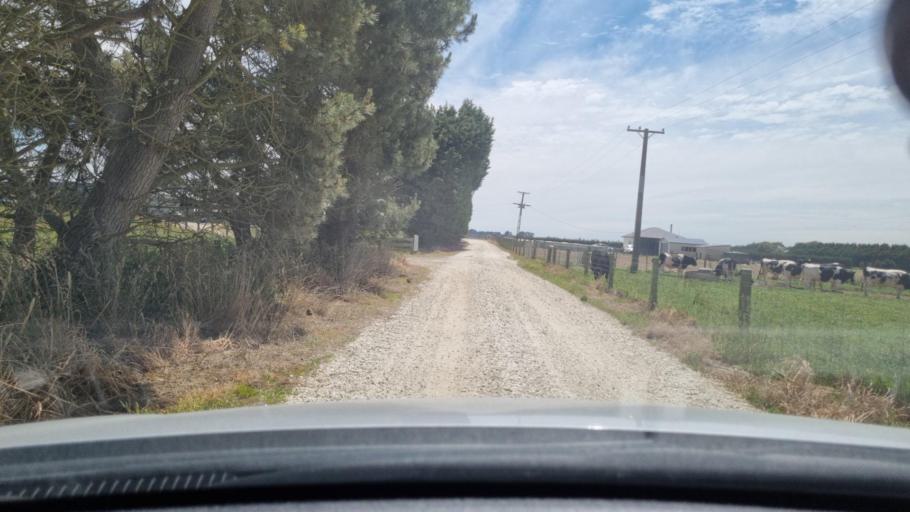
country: NZ
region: Southland
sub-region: Invercargill City
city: Invercargill
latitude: -46.3670
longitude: 168.2828
